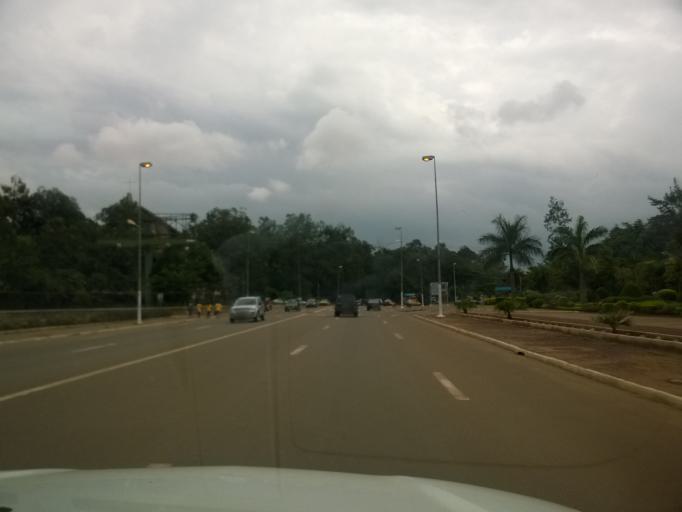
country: CM
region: Centre
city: Yaounde
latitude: 3.8684
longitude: 11.5146
